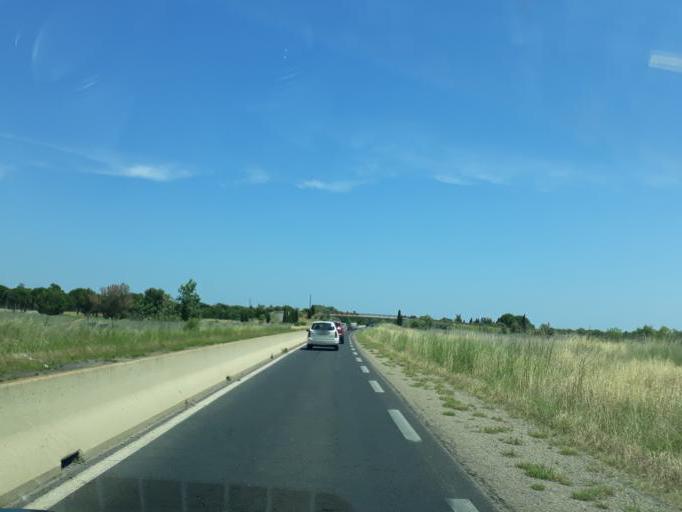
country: FR
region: Languedoc-Roussillon
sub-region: Departement de l'Herault
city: Vias
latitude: 43.3099
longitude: 3.4041
